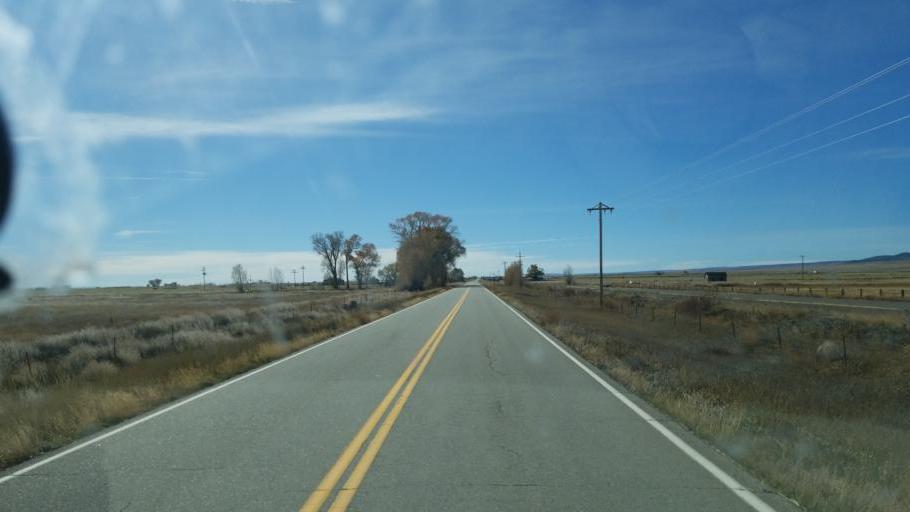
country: US
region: Colorado
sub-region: Rio Grande County
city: Monte Vista
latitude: 37.4613
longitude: -106.1485
